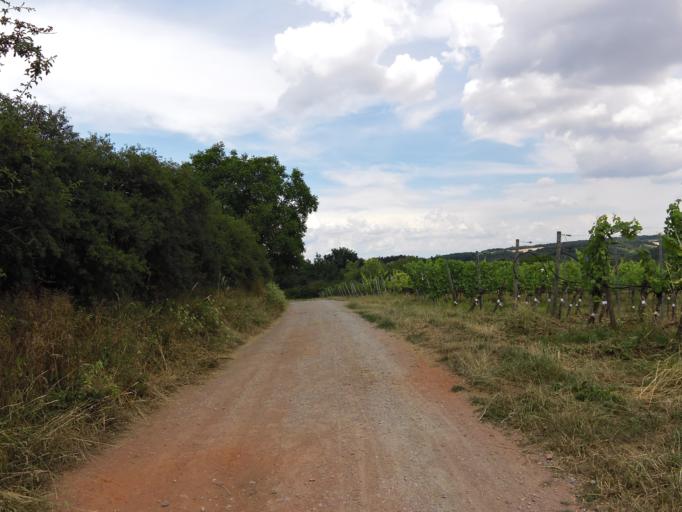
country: DE
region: Bavaria
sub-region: Regierungsbezirk Unterfranken
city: Randersacker
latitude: 49.7680
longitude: 9.9862
